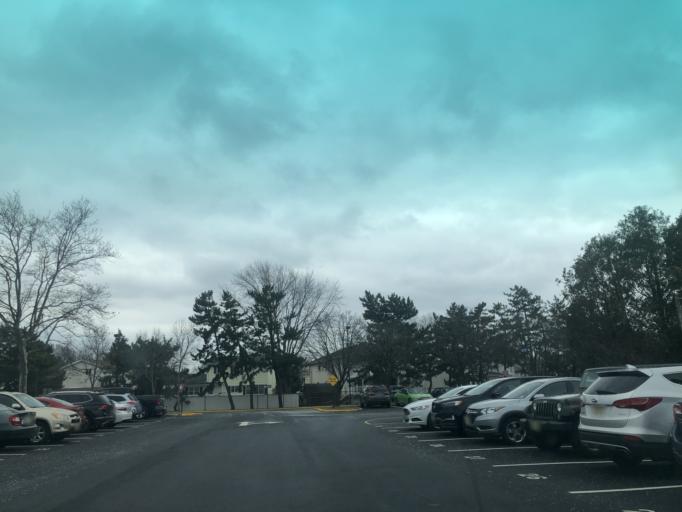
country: US
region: New Jersey
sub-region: Hudson County
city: Secaucus
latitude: 40.8038
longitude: -74.0520
